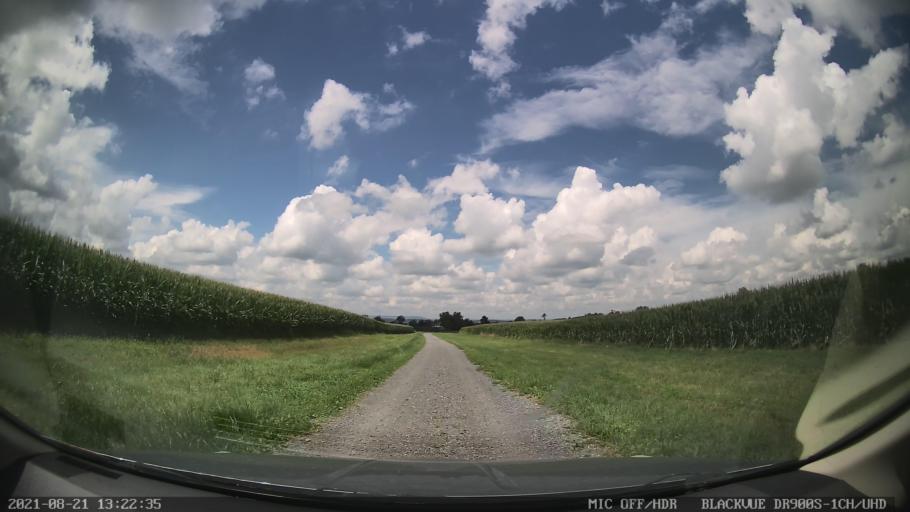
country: US
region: Pennsylvania
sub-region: Berks County
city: Fleetwood
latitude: 40.4678
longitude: -75.7784
